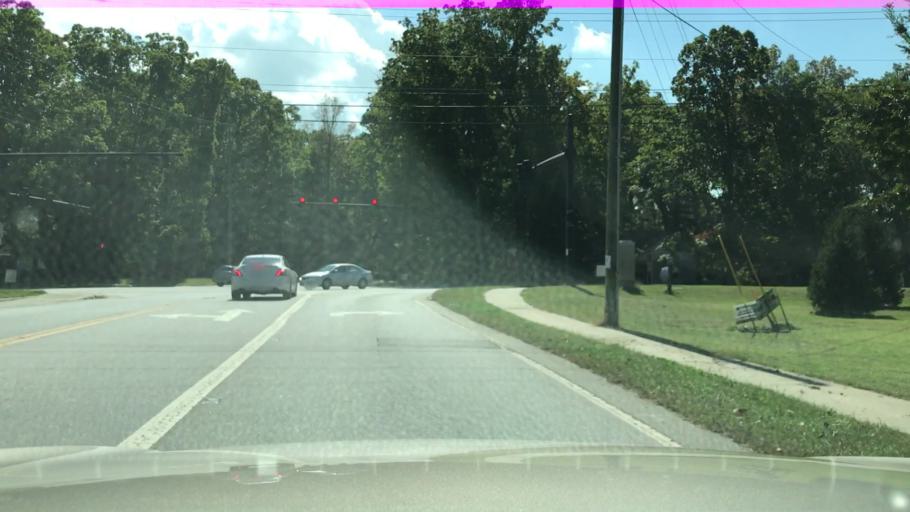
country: US
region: North Carolina
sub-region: Buncombe County
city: Royal Pines
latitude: 35.4836
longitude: -82.5386
